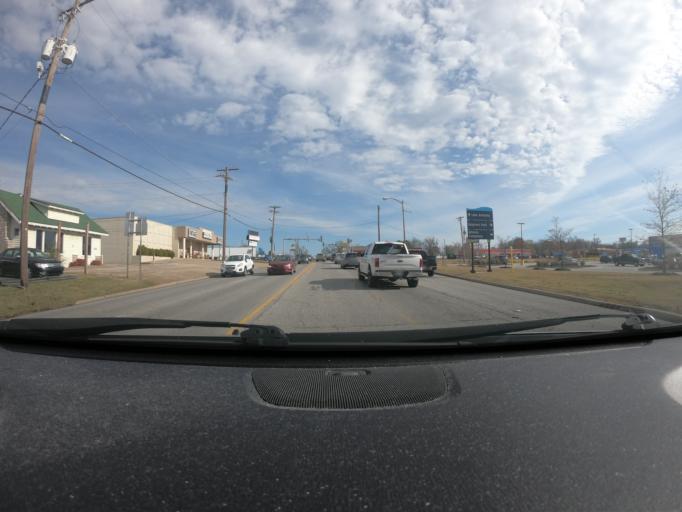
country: US
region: Arkansas
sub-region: Benton County
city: Rogers
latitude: 36.3335
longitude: -94.1269
